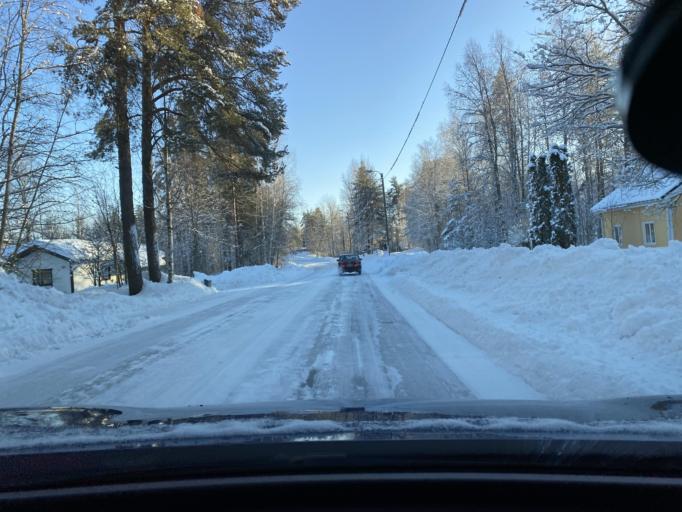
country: FI
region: Southern Savonia
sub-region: Mikkeli
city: Kangasniemi
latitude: 61.9961
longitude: 26.6309
